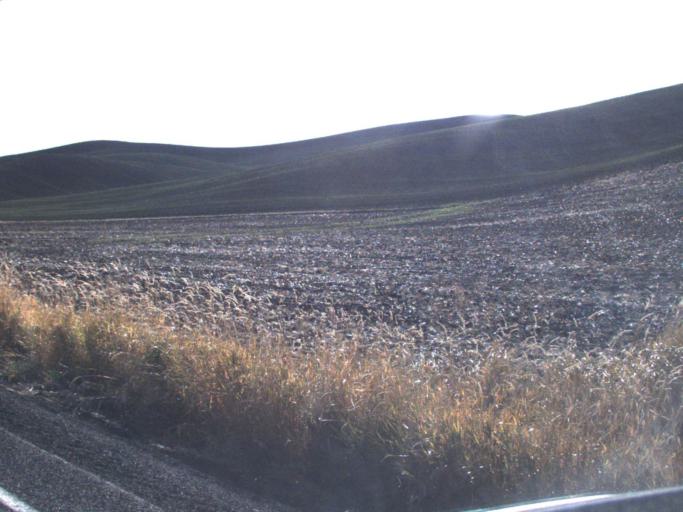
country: US
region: Washington
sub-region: Whitman County
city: Colfax
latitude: 46.7514
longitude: -117.3728
